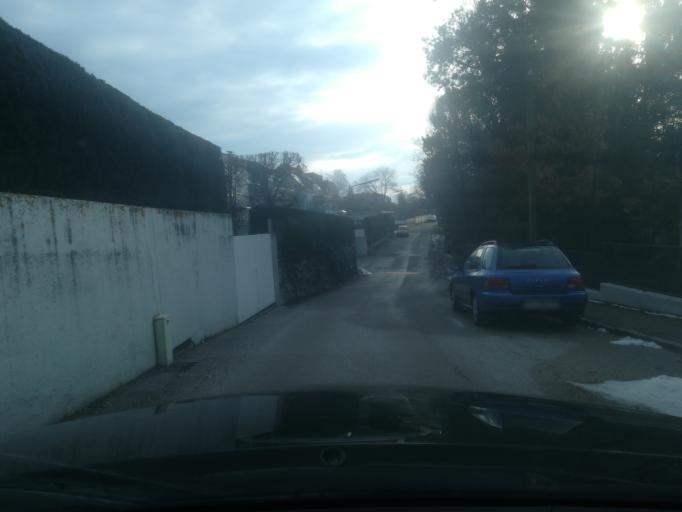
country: AT
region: Upper Austria
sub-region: Politischer Bezirk Linz-Land
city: Leonding
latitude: 48.2827
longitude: 14.2525
